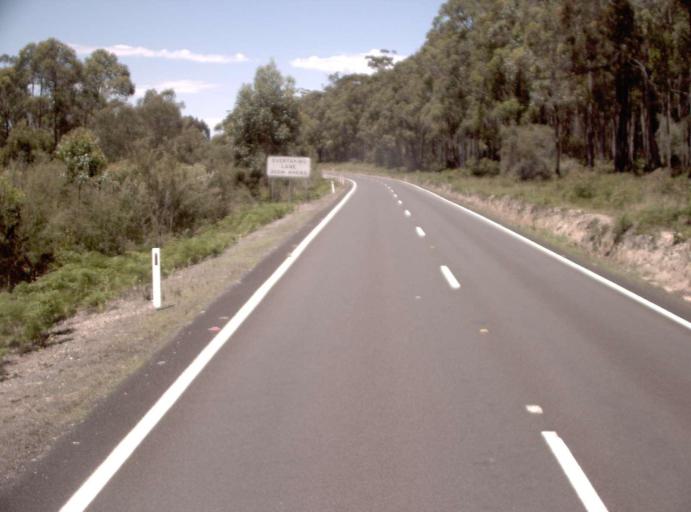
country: AU
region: Victoria
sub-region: East Gippsland
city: Lakes Entrance
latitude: -37.7106
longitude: 148.6771
